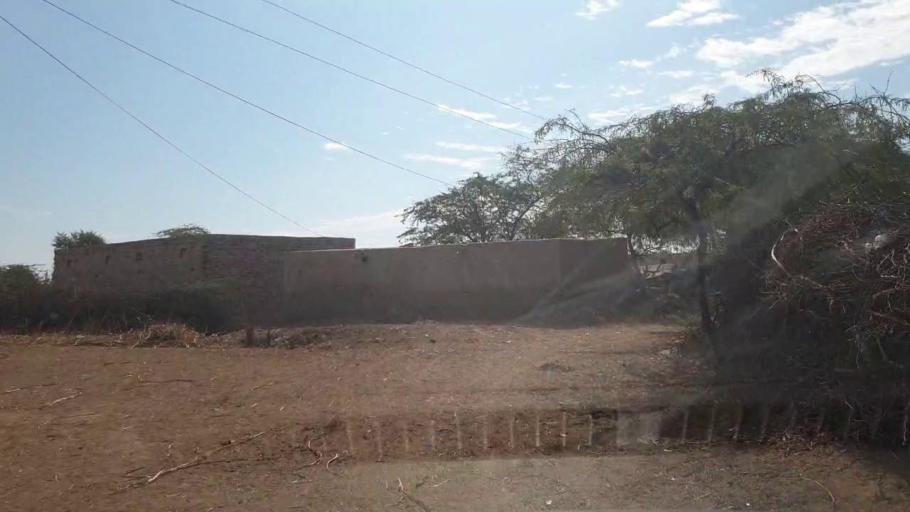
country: PK
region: Sindh
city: Sanghar
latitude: 26.0407
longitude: 68.9250
